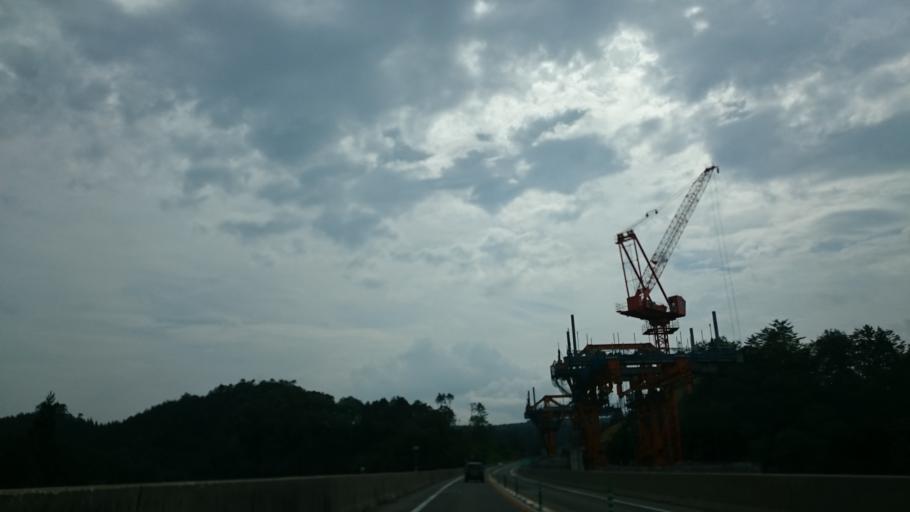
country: JP
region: Gifu
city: Gujo
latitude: 36.0200
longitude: 136.9433
